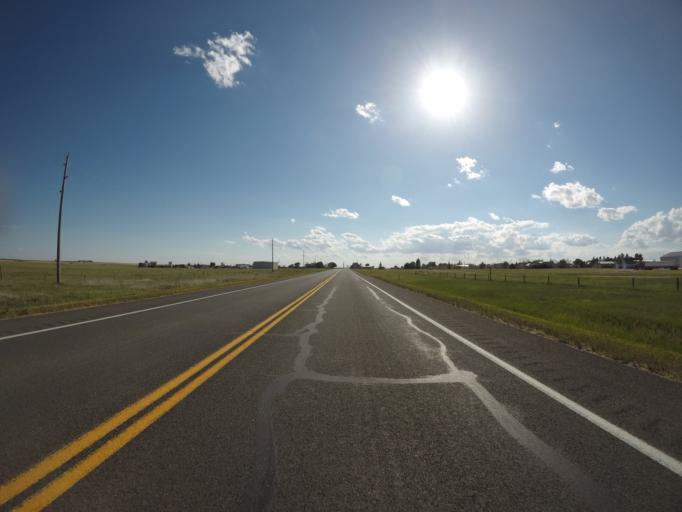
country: US
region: Colorado
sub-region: Morgan County
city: Fort Morgan
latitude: 40.6083
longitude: -103.8359
